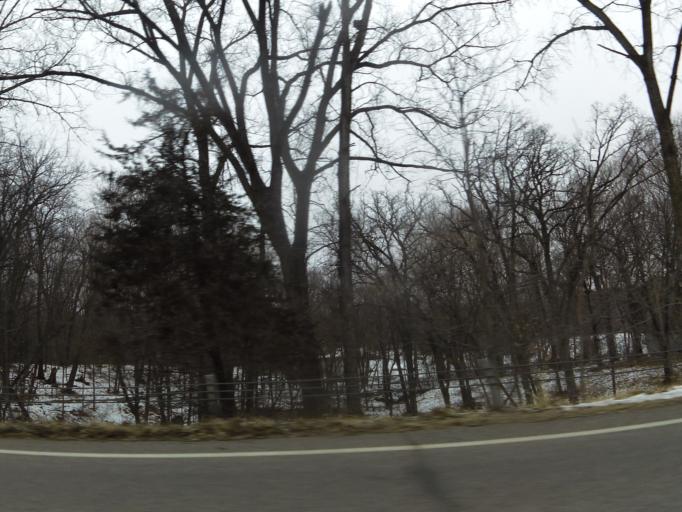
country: US
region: Minnesota
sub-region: Scott County
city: Jordan
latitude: 44.6307
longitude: -93.5977
